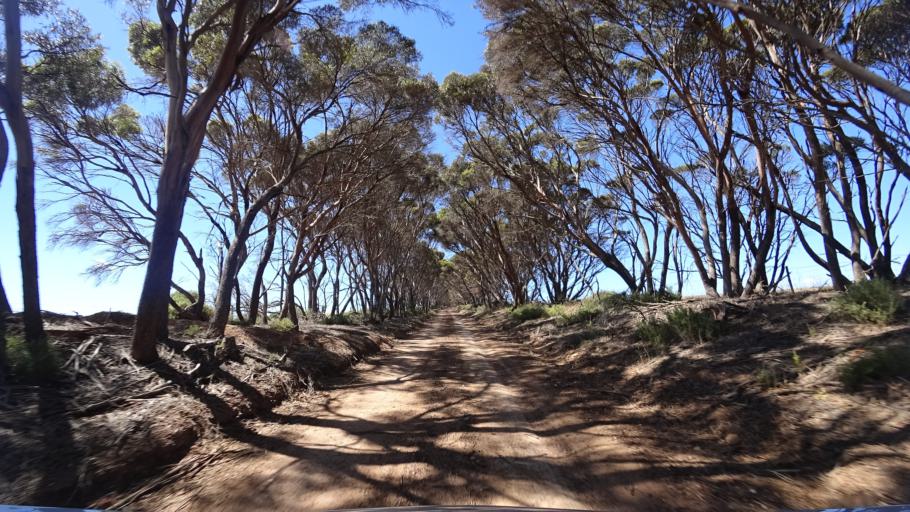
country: AU
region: South Australia
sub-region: Kangaroo Island
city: Kingscote
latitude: -35.7417
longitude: 137.7213
